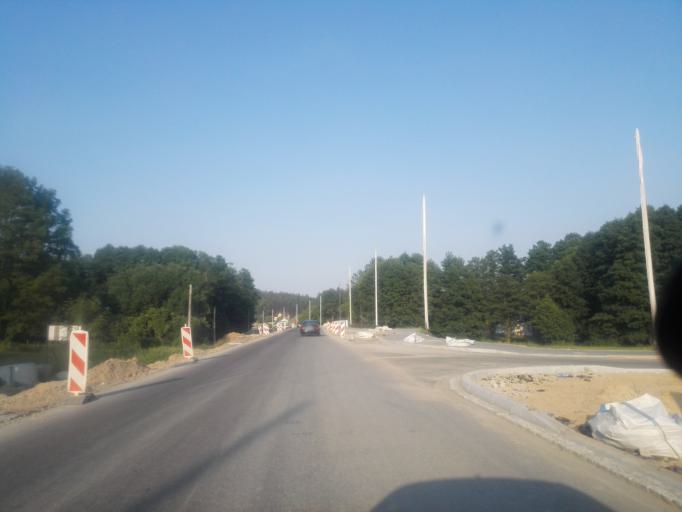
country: PL
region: Podlasie
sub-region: Powiat sejnenski
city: Krasnopol
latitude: 54.0826
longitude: 23.0888
